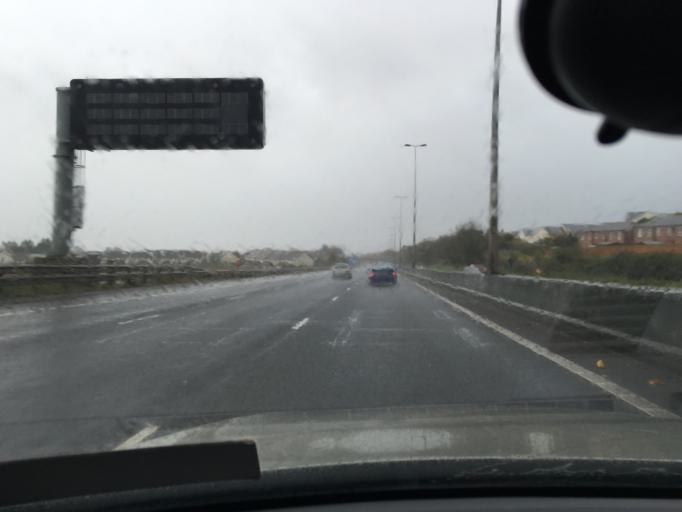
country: GB
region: Northern Ireland
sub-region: Newtownabbey District
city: Newtownabbey
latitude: 54.6584
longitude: -5.9345
